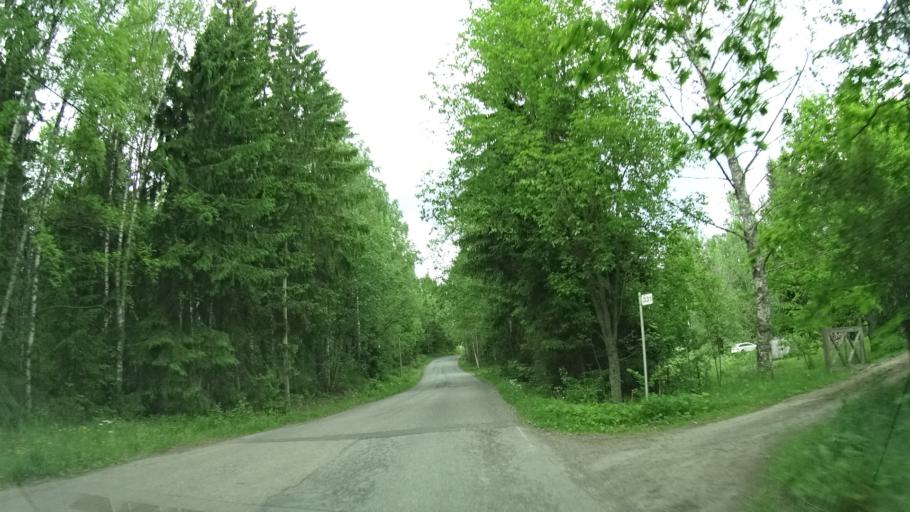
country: FI
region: Uusimaa
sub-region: Helsinki
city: Siuntio
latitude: 60.2088
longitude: 24.2377
